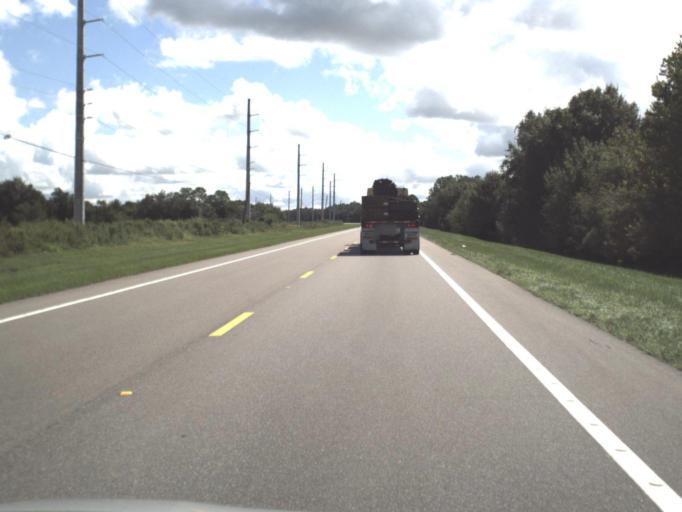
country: US
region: Florida
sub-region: Sarasota County
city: The Meadows
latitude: 27.4223
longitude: -82.3690
